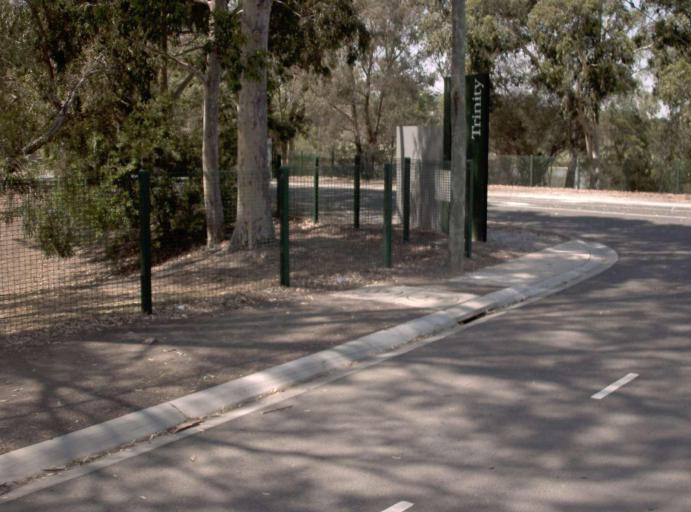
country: AU
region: Victoria
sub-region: Manningham
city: Bulleen
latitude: -37.7704
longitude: 145.0793
